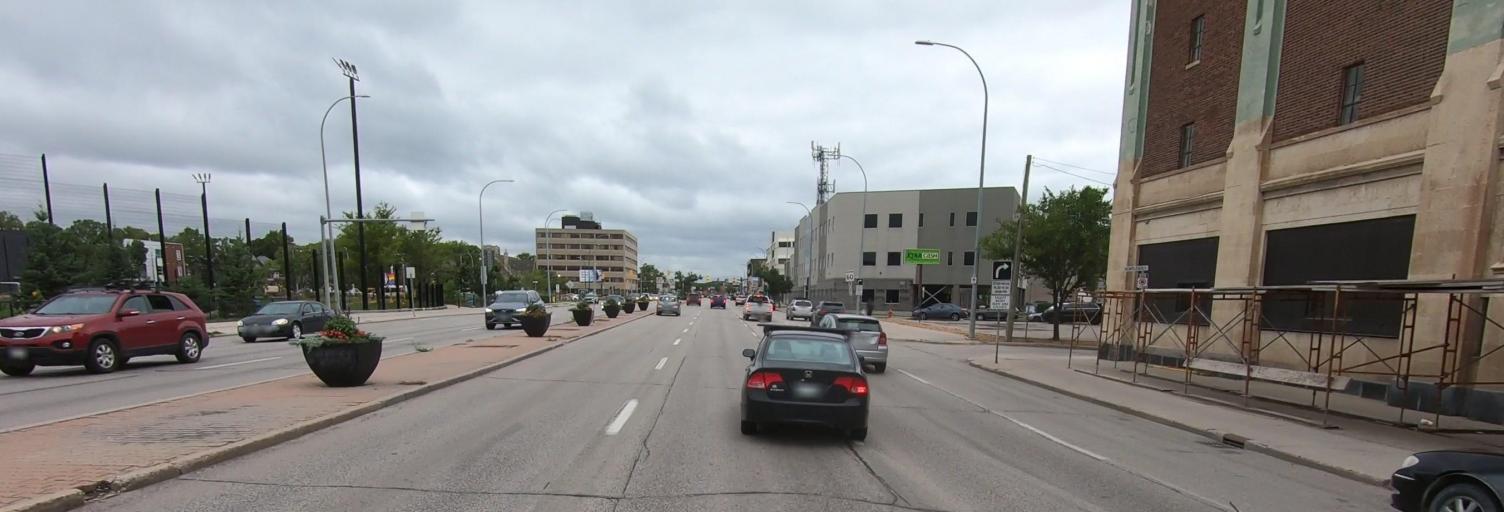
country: CA
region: Manitoba
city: Winnipeg
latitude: 49.8876
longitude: -97.1626
